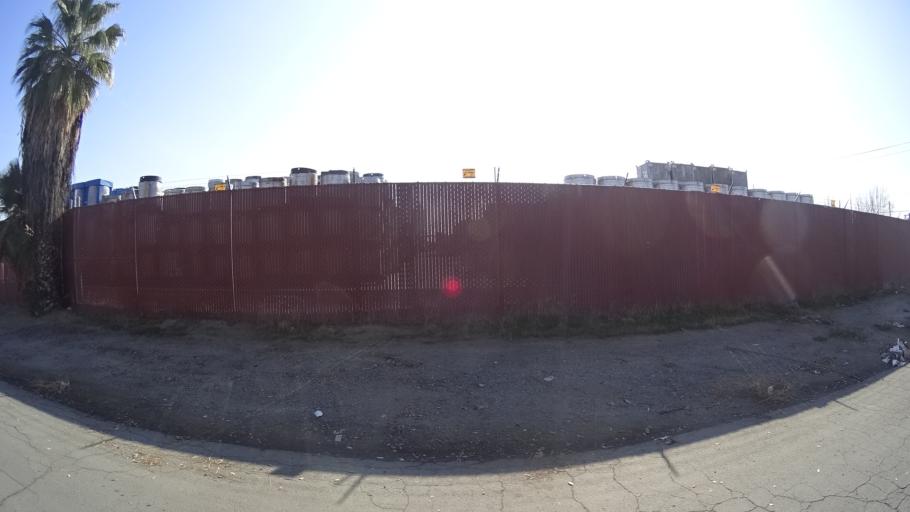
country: US
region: California
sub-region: Kern County
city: Bakersfield
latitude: 35.3588
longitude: -119.0047
